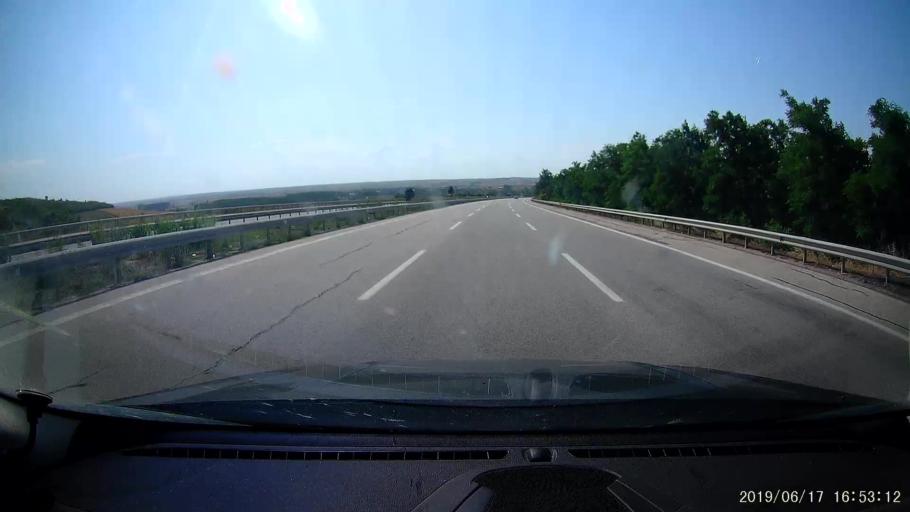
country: TR
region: Kirklareli
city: Inece
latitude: 41.5610
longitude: 27.0296
